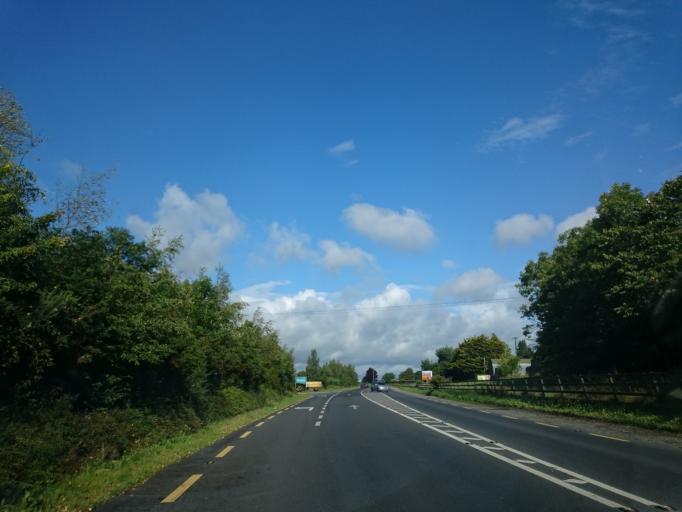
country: IE
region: Leinster
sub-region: Kilkenny
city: Kilkenny
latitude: 52.6953
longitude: -7.2622
